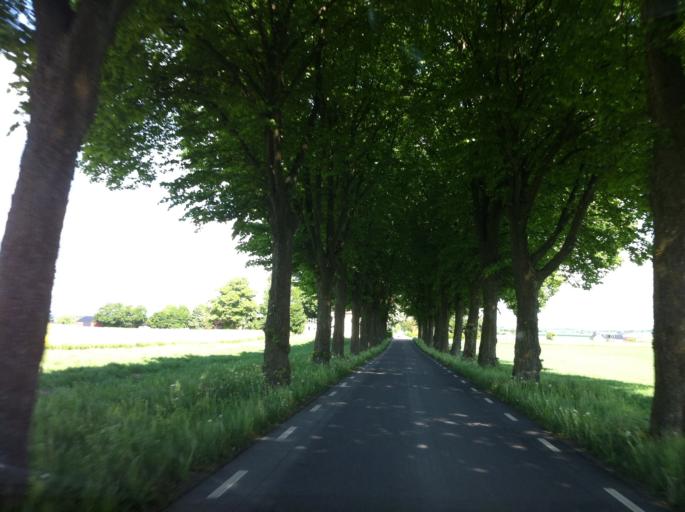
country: SE
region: Skane
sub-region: Landskrona
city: Asmundtorp
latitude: 55.9617
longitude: 12.9055
